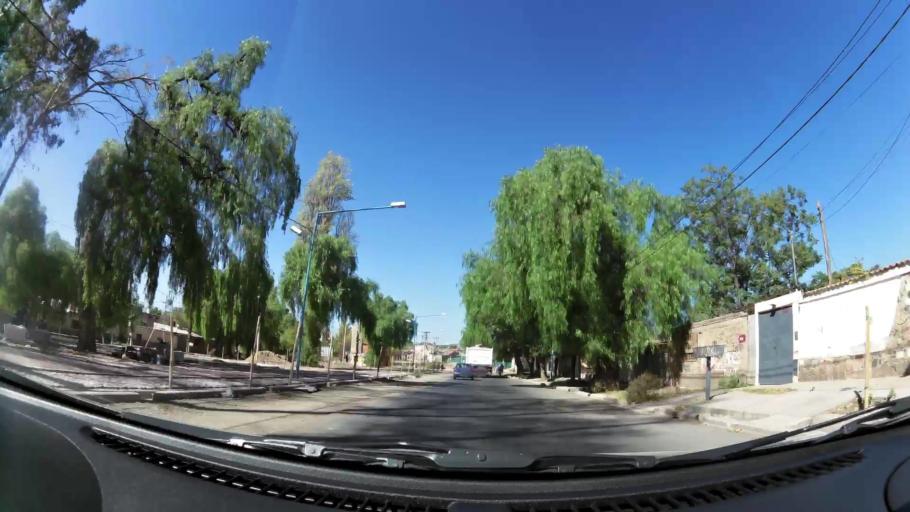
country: AR
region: Mendoza
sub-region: Departamento de Godoy Cruz
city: Godoy Cruz
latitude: -32.9081
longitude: -68.8795
